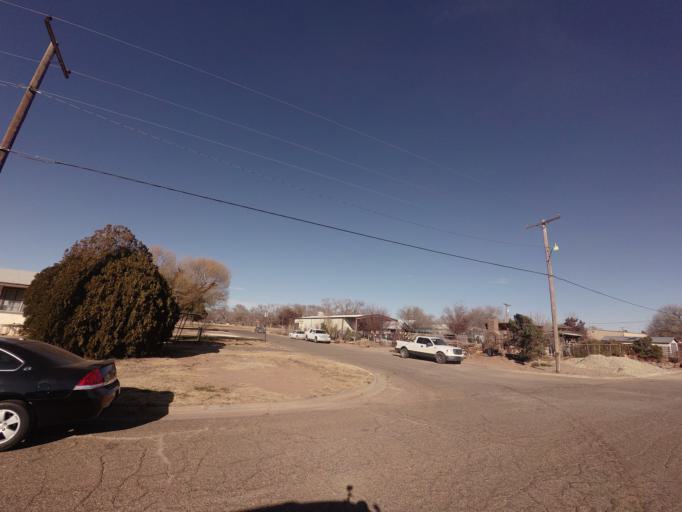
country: US
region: New Mexico
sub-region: Curry County
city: Clovis
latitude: 34.4039
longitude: -103.1815
